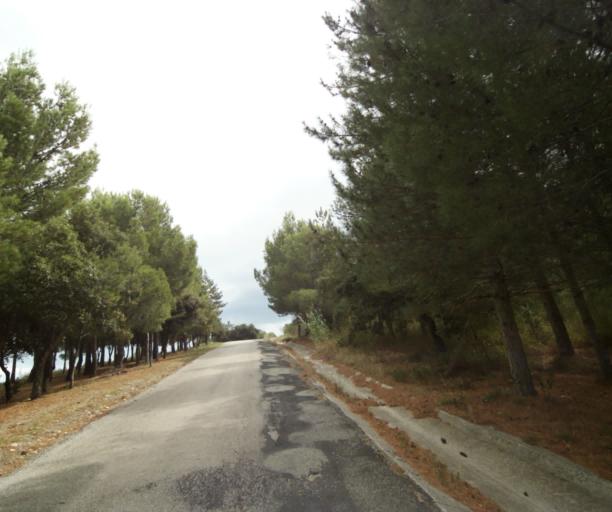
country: FR
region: Languedoc-Roussillon
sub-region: Departement des Pyrenees-Orientales
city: Collioure
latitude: 42.5303
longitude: 3.0553
